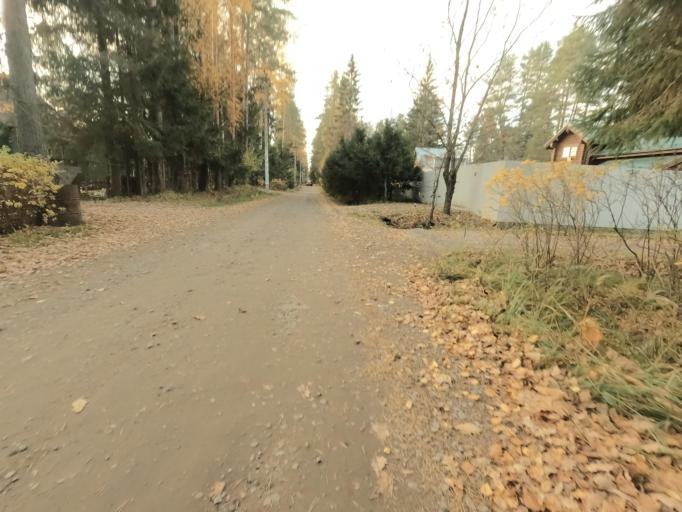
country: RU
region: St.-Petersburg
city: Beloostrov
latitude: 60.1672
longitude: 29.9909
